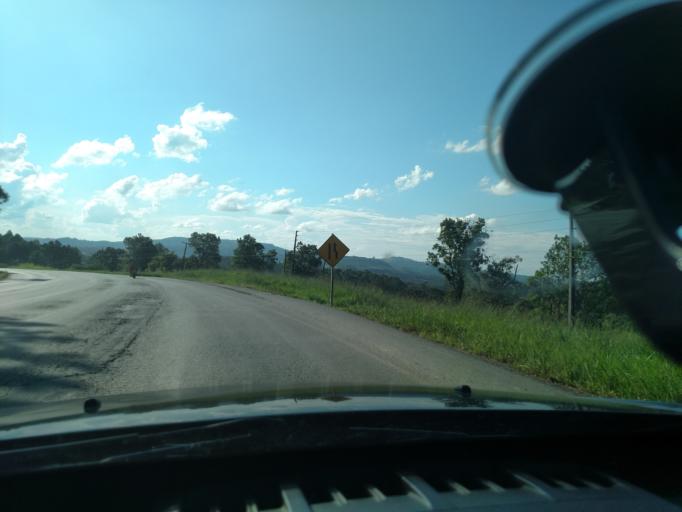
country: BR
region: Santa Catarina
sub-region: Otacilio Costa
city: Otacilio Costa
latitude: -27.2534
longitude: -49.9495
